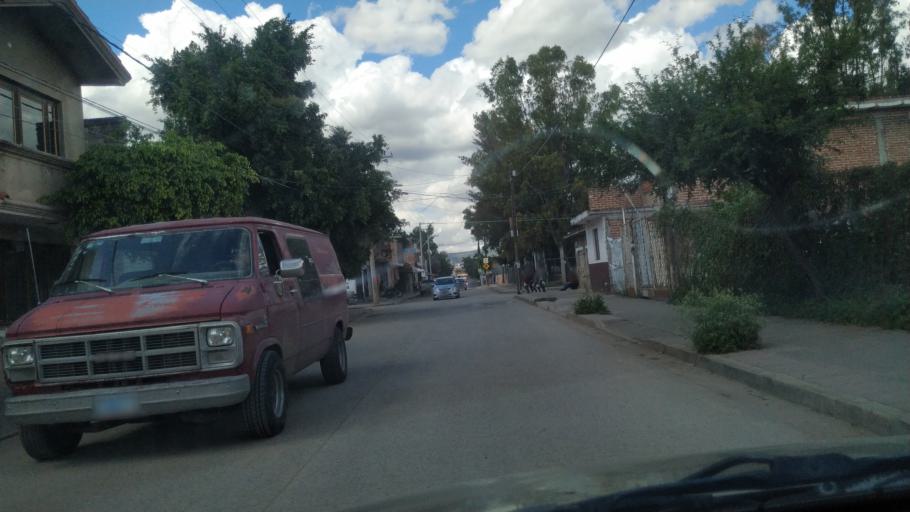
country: MX
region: Guanajuato
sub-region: Leon
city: Medina
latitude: 21.1458
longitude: -101.6291
